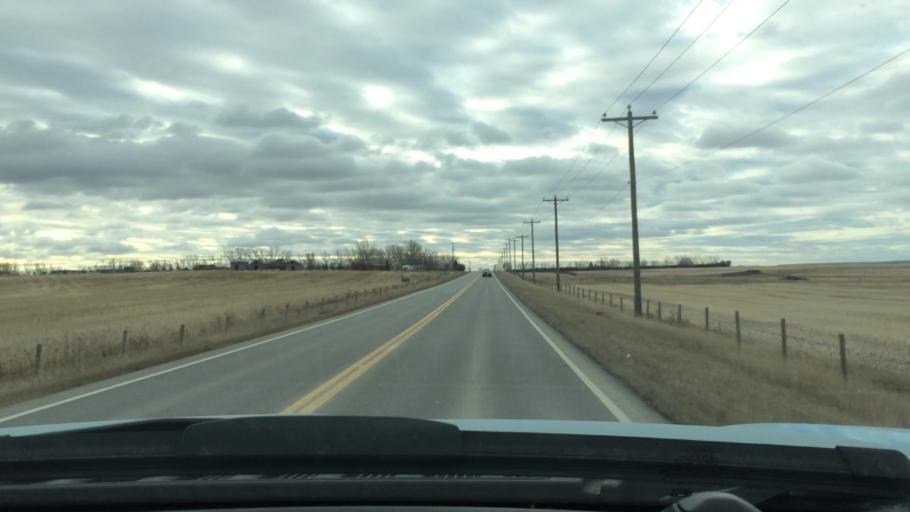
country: CA
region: Alberta
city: Airdrie
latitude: 51.2367
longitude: -114.0250
